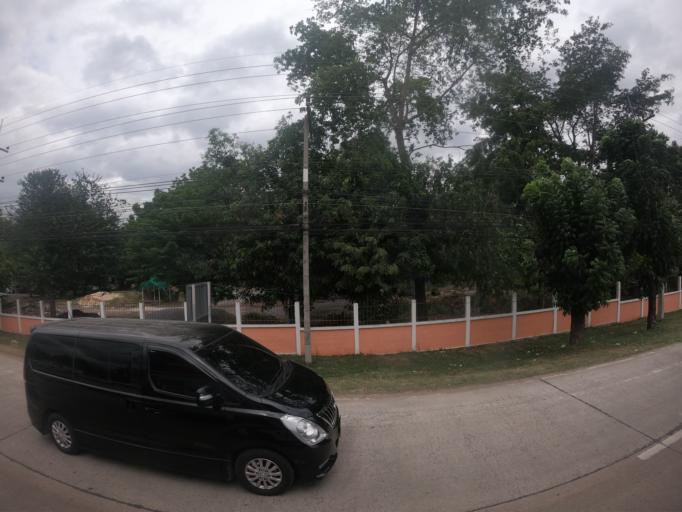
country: TH
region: Nakhon Ratchasima
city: Chok Chai
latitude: 14.8462
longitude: 102.1893
